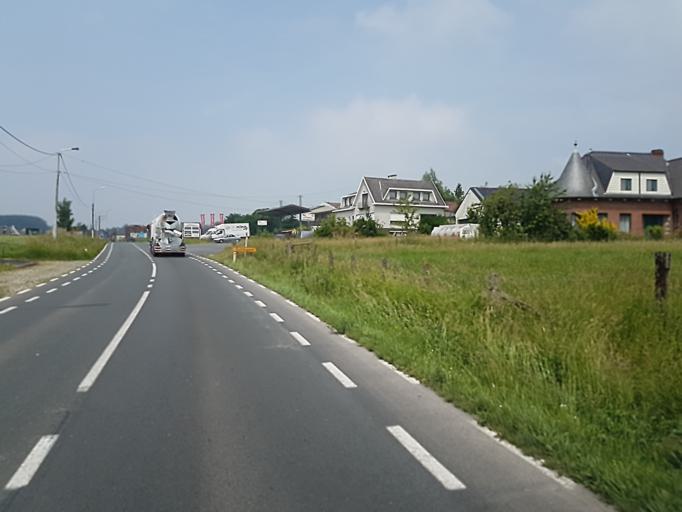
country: BE
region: Flanders
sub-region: Provincie Oost-Vlaanderen
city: Perre
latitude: 50.8609
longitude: 3.8565
